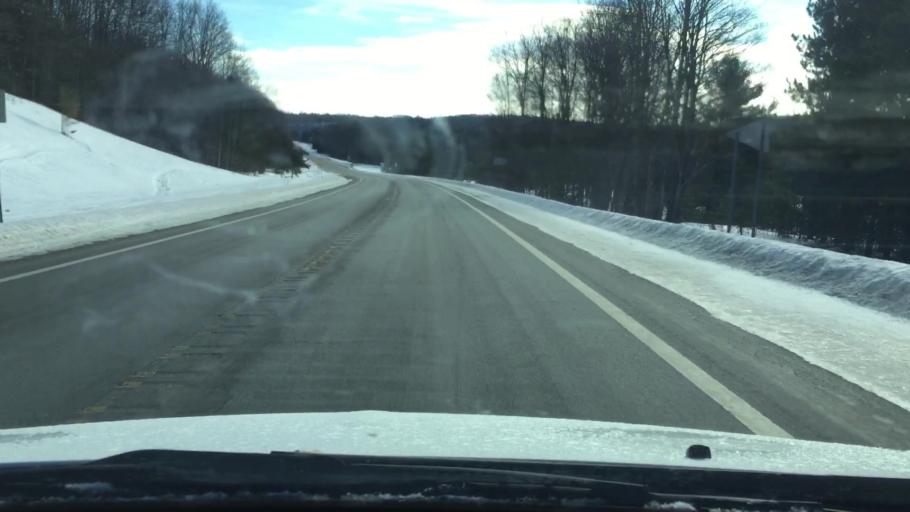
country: US
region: Michigan
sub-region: Antrim County
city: Mancelona
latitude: 44.9708
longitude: -85.0548
